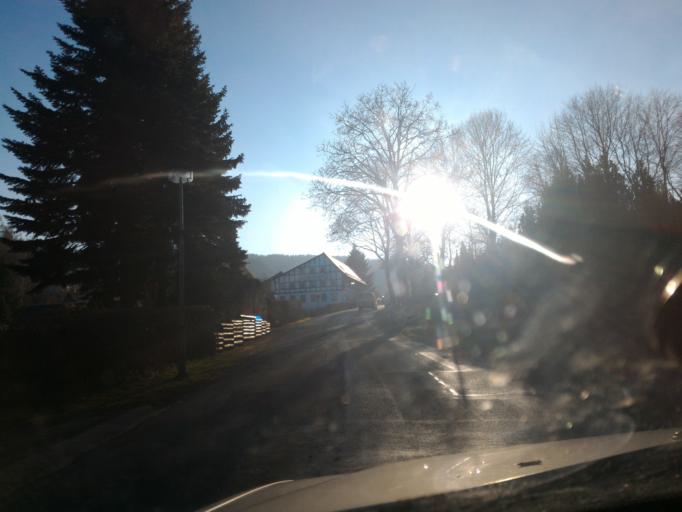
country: DE
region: Saxony
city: Kurort Jonsdorf
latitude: 50.8545
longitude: 14.6915
